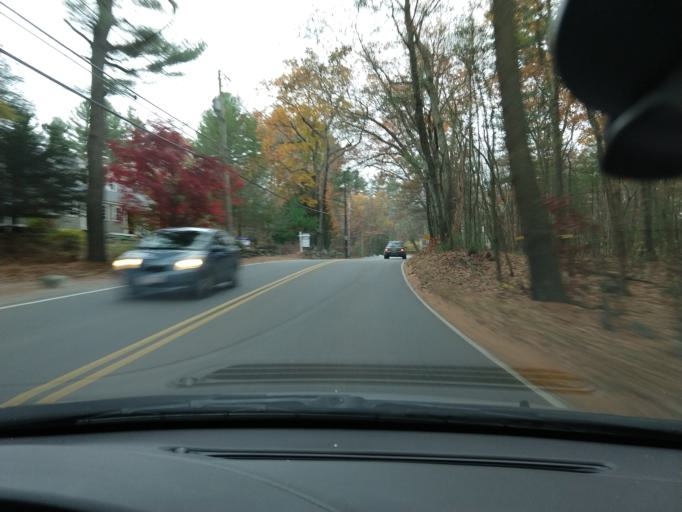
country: US
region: Massachusetts
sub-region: Middlesex County
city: Carlisle
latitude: 42.5368
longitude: -71.3494
